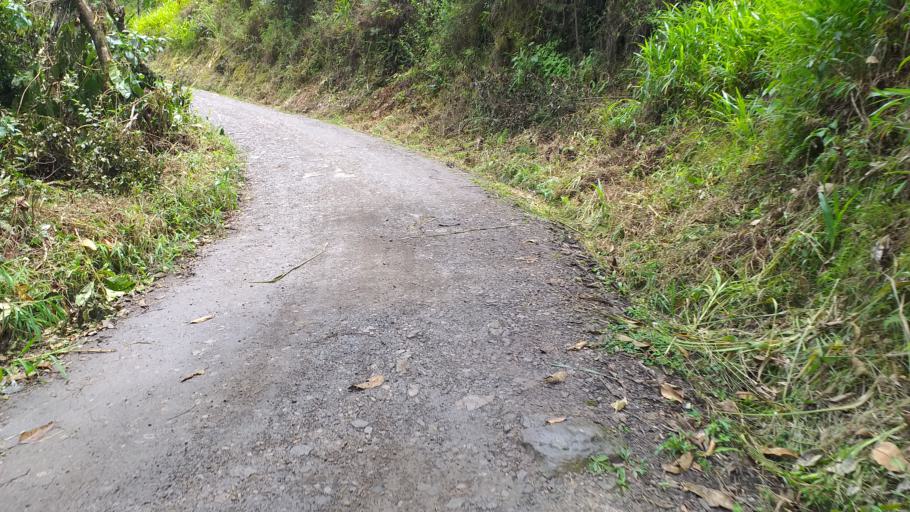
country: CO
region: Cundinamarca
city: Tenza
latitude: 5.1134
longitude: -73.4524
